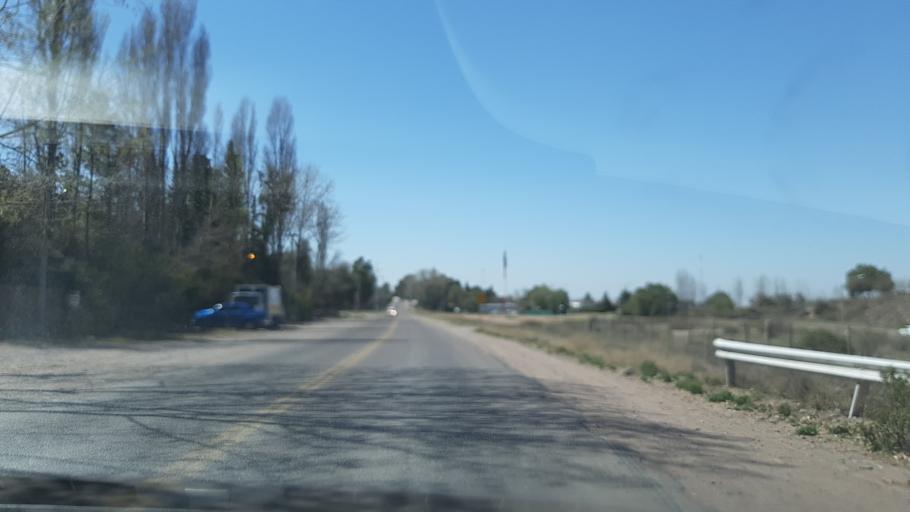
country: AR
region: Mendoza
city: Lujan de Cuyo
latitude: -33.0165
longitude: -68.9338
